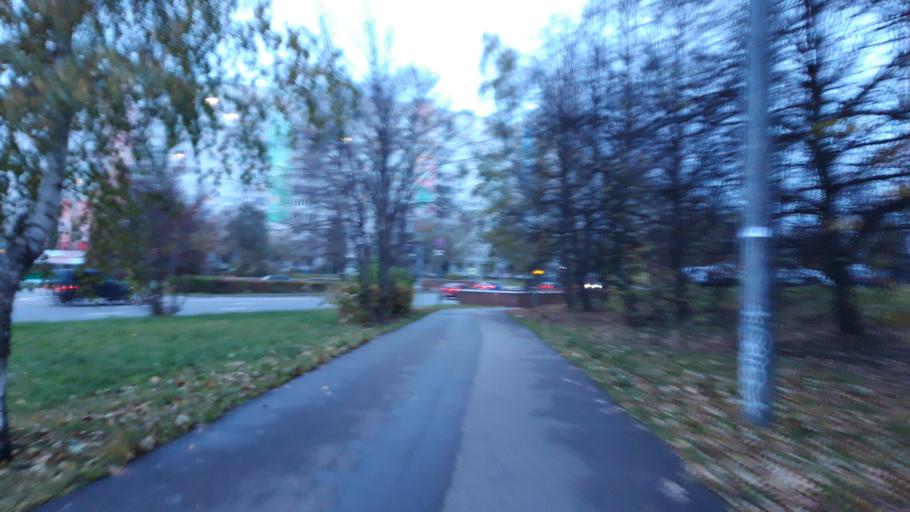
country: RU
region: Moscow
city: Zelenograd
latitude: 55.9828
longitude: 37.1793
